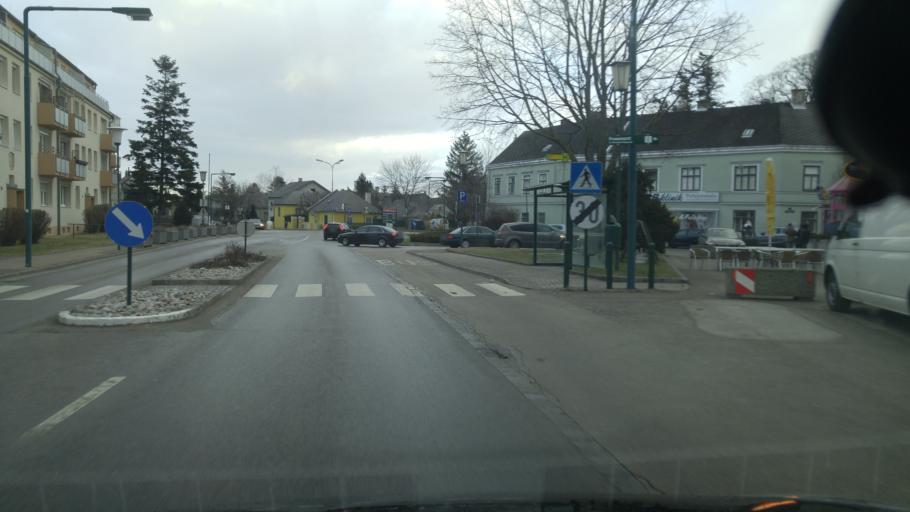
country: AT
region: Lower Austria
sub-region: Politischer Bezirk Baden
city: Bad Voslau
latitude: 47.9637
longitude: 16.2159
